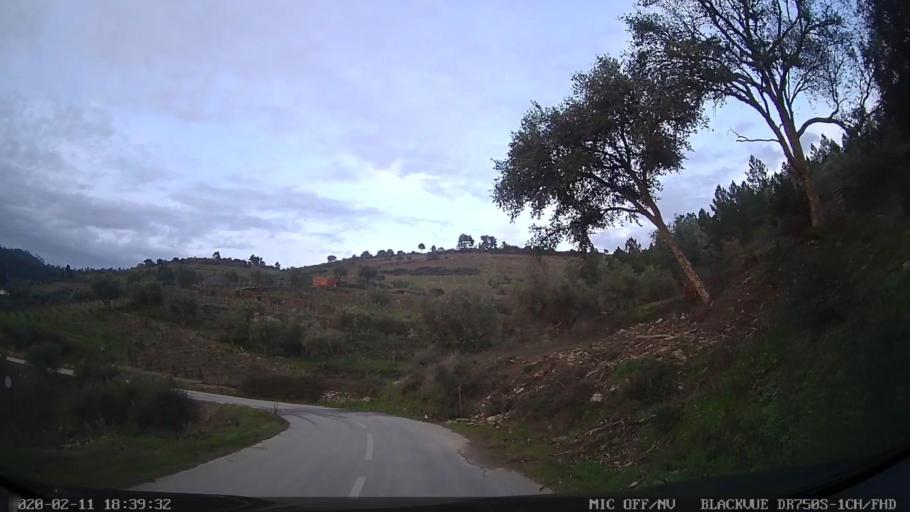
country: PT
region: Vila Real
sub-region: Sabrosa
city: Vilela
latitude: 41.1779
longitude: -7.5952
